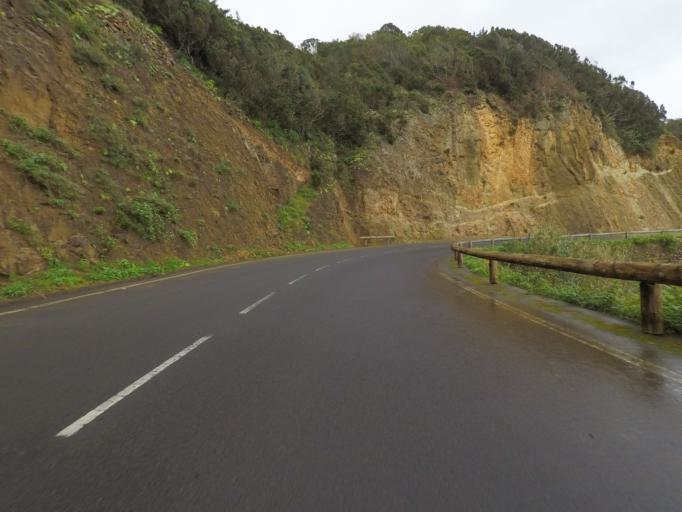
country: ES
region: Canary Islands
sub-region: Provincia de Santa Cruz de Tenerife
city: Agulo
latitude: 28.1912
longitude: -17.2292
